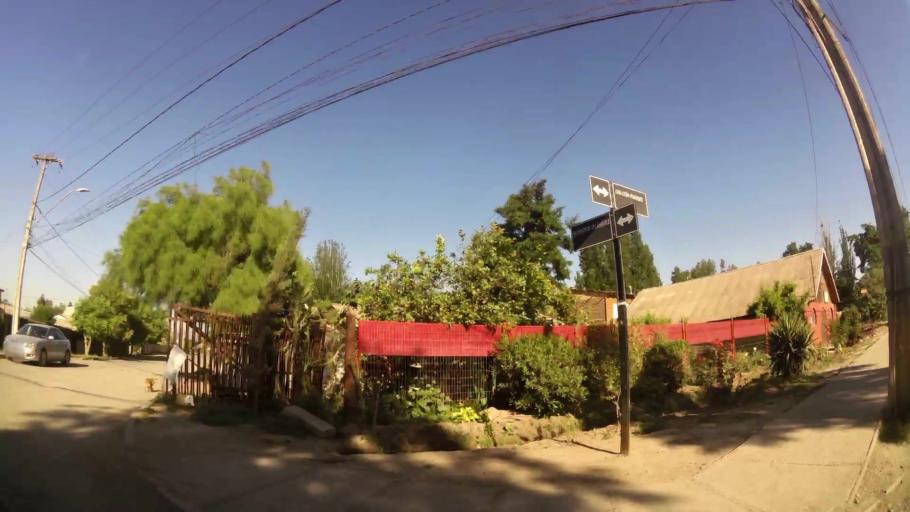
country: CL
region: Santiago Metropolitan
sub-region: Provincia de Maipo
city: San Bernardo
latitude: -33.6444
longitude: -70.6908
